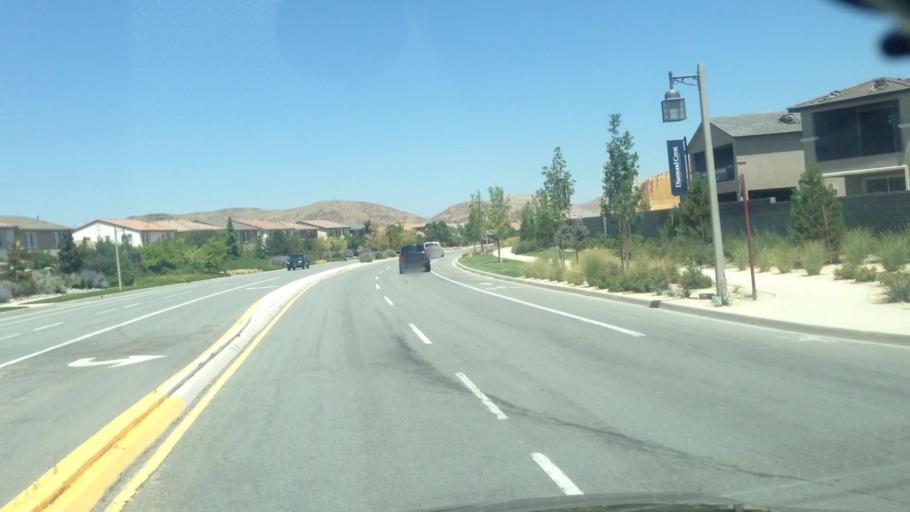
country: US
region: Nevada
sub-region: Washoe County
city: Sparks
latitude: 39.4469
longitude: -119.7277
